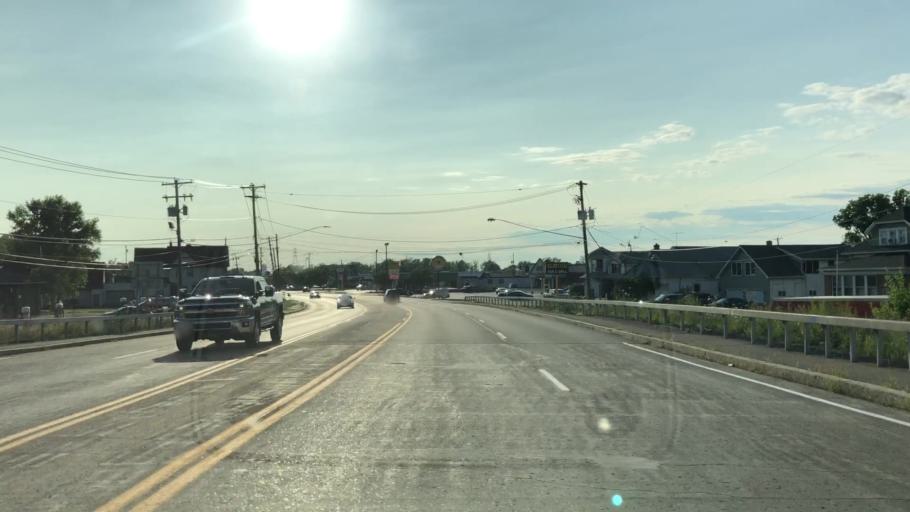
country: US
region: New York
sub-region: Erie County
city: Sloan
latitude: 42.8712
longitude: -78.7839
